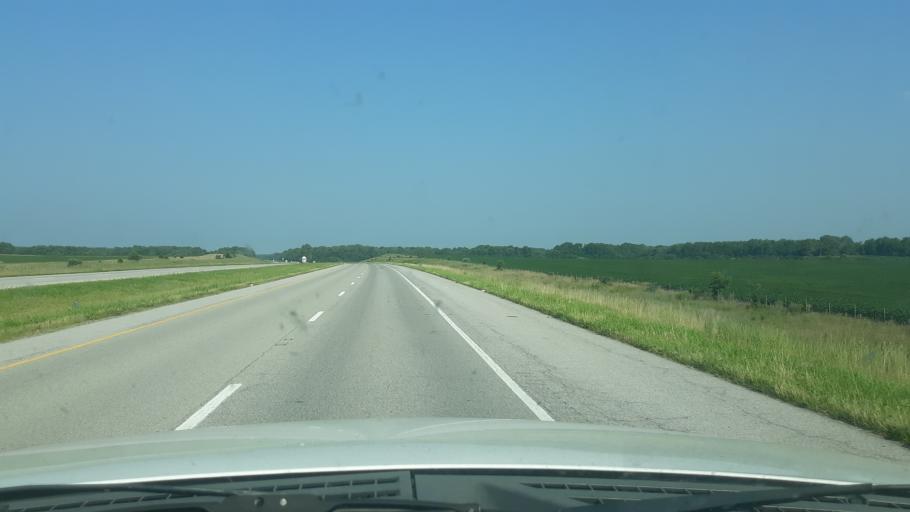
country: US
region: Illinois
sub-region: Saline County
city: Carrier Mills
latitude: 37.7326
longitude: -88.6126
